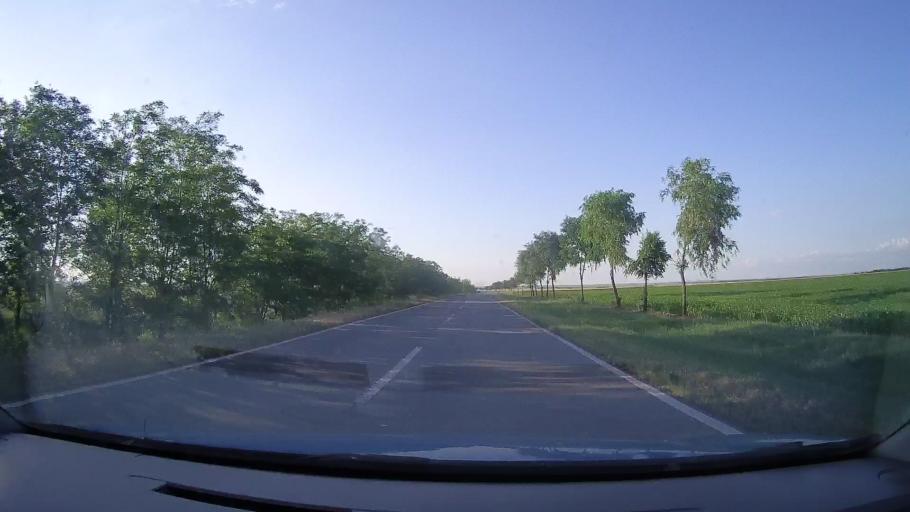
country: RO
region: Timis
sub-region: Comuna Moravita
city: Moravita
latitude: 45.2070
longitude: 21.2998
